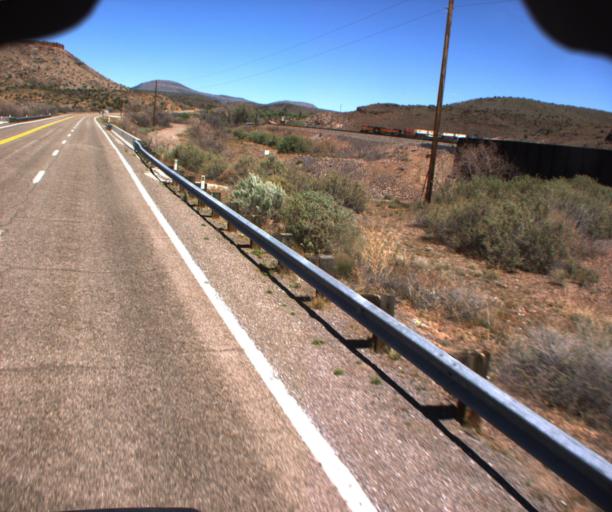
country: US
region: Arizona
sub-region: Mohave County
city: Peach Springs
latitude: 35.4219
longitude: -113.6486
